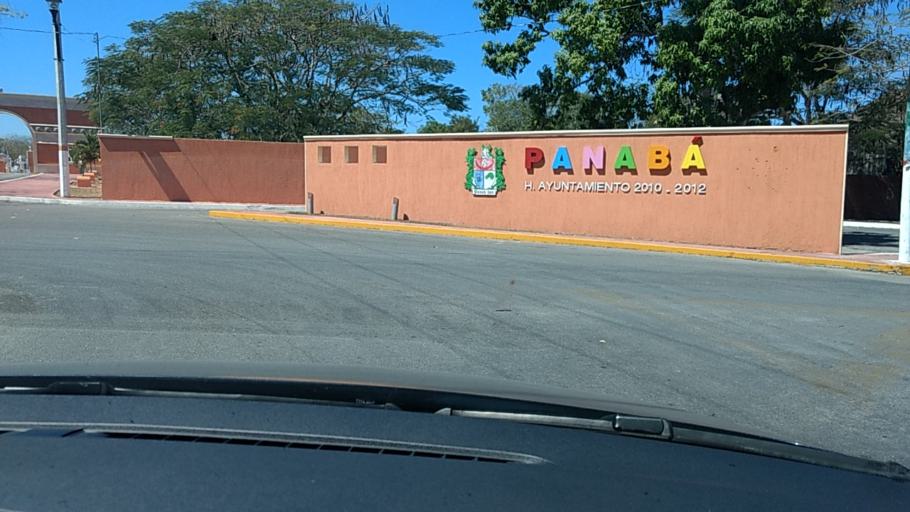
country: MX
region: Yucatan
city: Panaba
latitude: 21.2904
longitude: -88.2729
